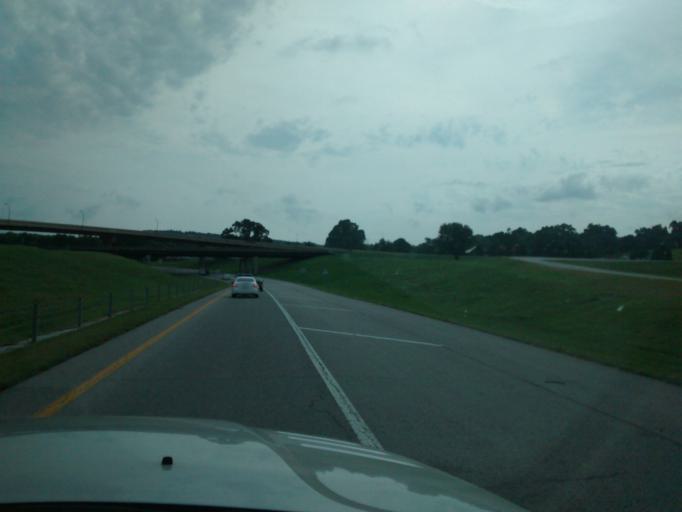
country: US
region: Arkansas
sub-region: Washington County
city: Johnson
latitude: 36.1164
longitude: -94.1480
